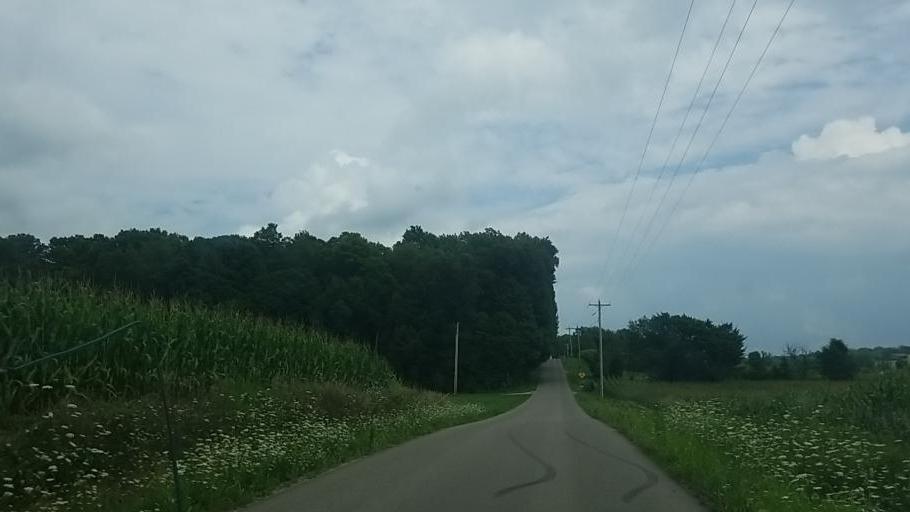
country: US
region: Ohio
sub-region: Licking County
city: Utica
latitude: 40.2470
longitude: -82.3239
